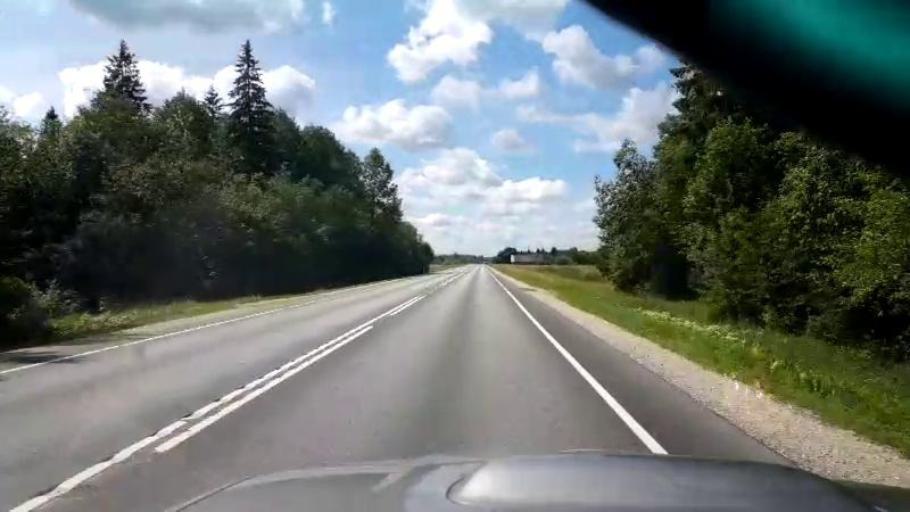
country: EE
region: Laeaene-Virumaa
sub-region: Tapa vald
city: Tapa
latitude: 59.2745
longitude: 26.0386
